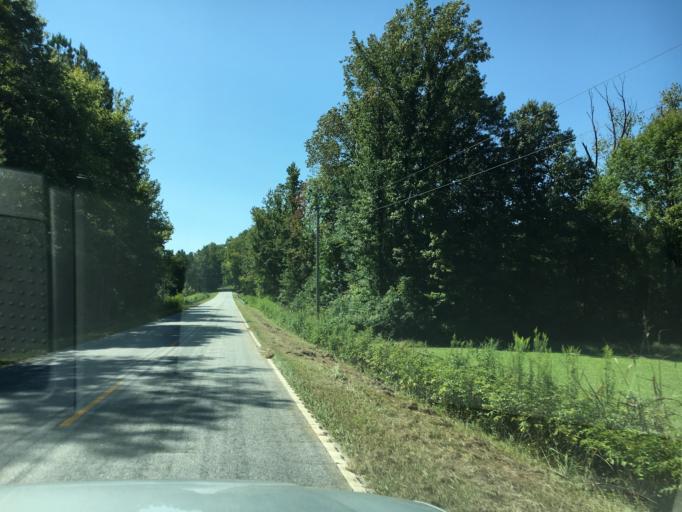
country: US
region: South Carolina
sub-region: Laurens County
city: Clinton
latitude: 34.4249
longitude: -81.8681
